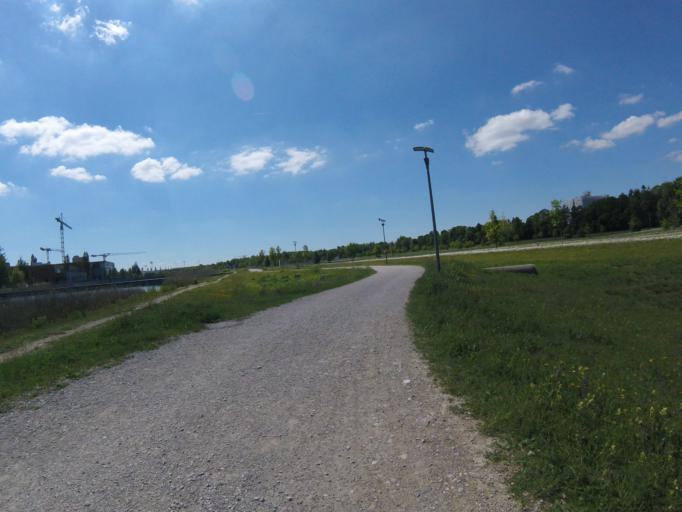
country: DE
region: Bavaria
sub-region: Upper Bavaria
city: Unterhaching
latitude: 48.0794
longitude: 11.6119
